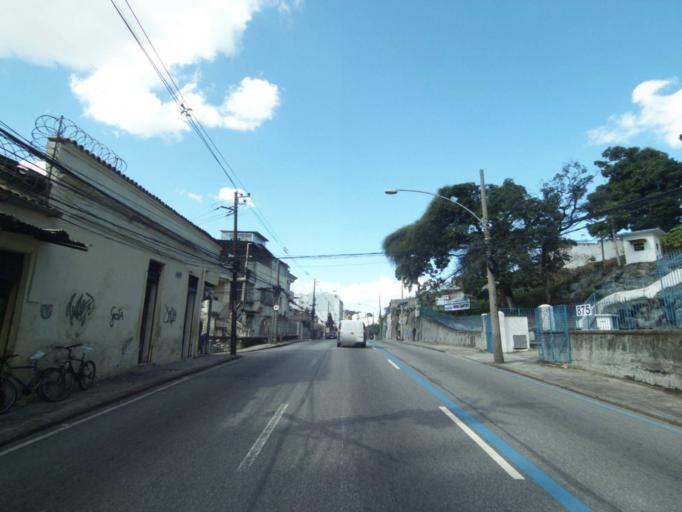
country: BR
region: Rio de Janeiro
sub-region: Rio De Janeiro
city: Rio de Janeiro
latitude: -22.9030
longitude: -43.2479
